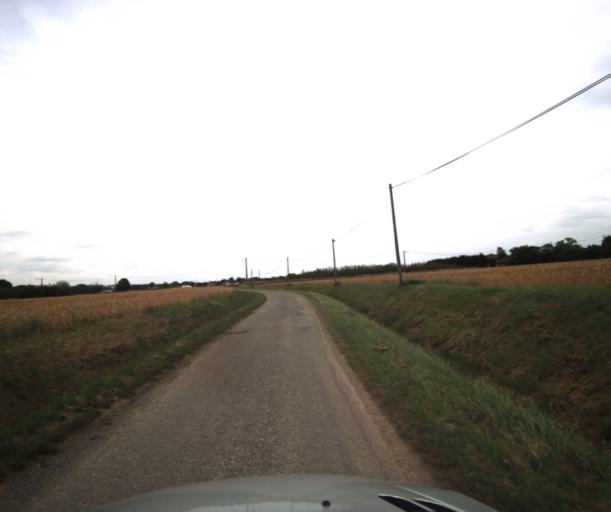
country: FR
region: Midi-Pyrenees
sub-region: Departement de la Haute-Garonne
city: Labarthe-sur-Leze
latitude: 43.4495
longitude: 1.3862
